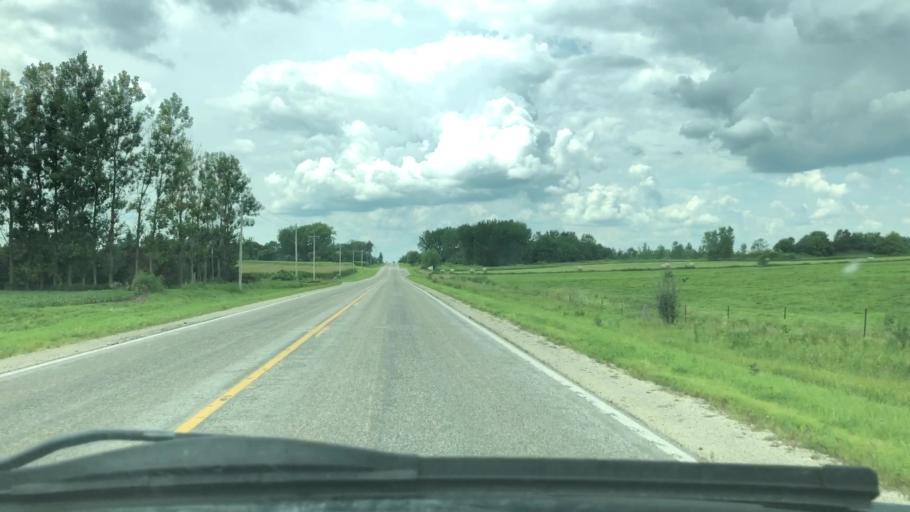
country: US
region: Minnesota
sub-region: Olmsted County
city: Stewartville
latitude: 43.8627
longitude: -92.5120
